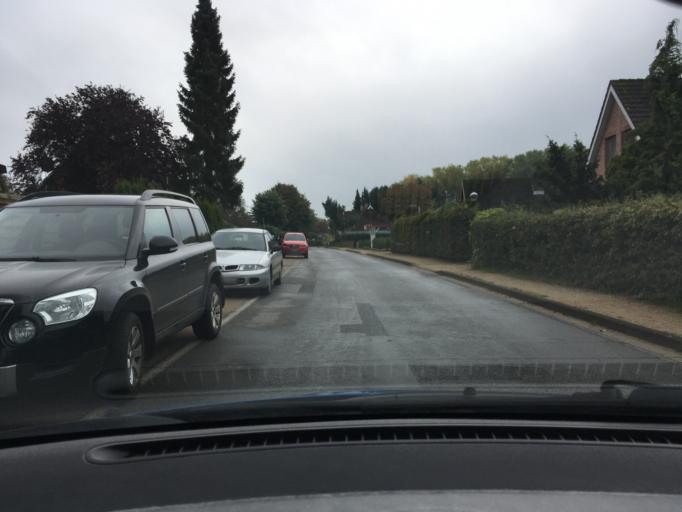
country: DE
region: Schleswig-Holstein
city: Bosau
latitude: 54.1040
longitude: 10.4296
